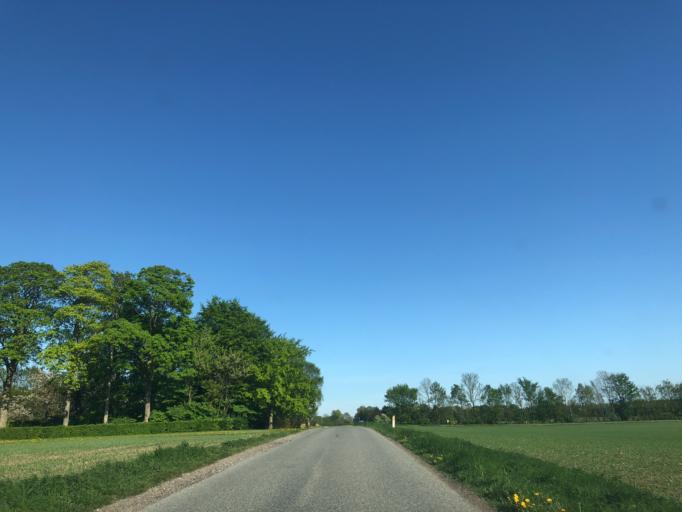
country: DK
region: Zealand
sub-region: Ringsted Kommune
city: Ringsted
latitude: 55.4502
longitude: 11.7193
